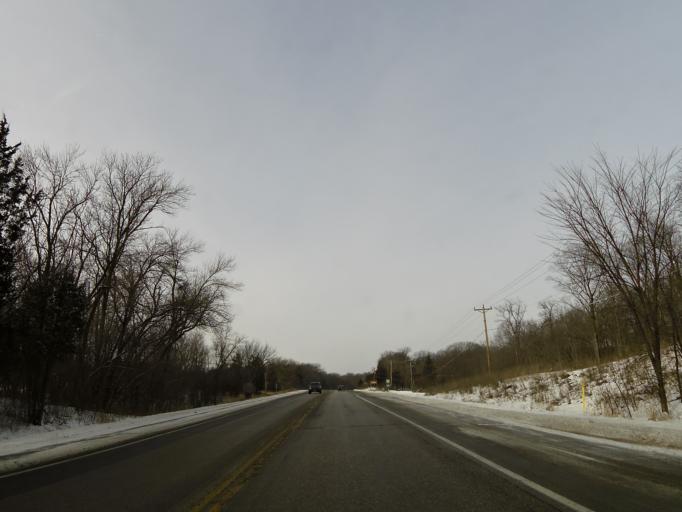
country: US
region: Minnesota
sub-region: Carver County
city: Victoria
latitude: 44.8863
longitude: -93.6510
